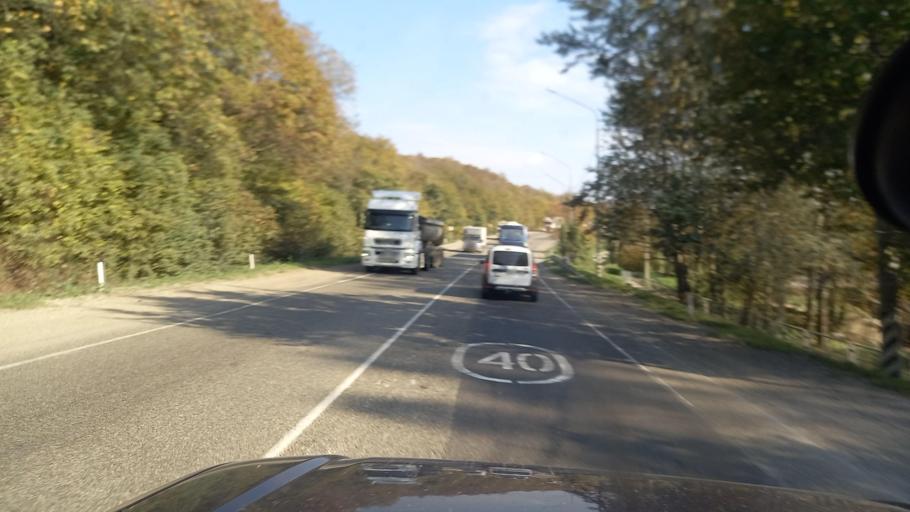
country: RU
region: Krasnodarskiy
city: Verkhnebakanskiy
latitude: 44.8614
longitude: 37.7368
